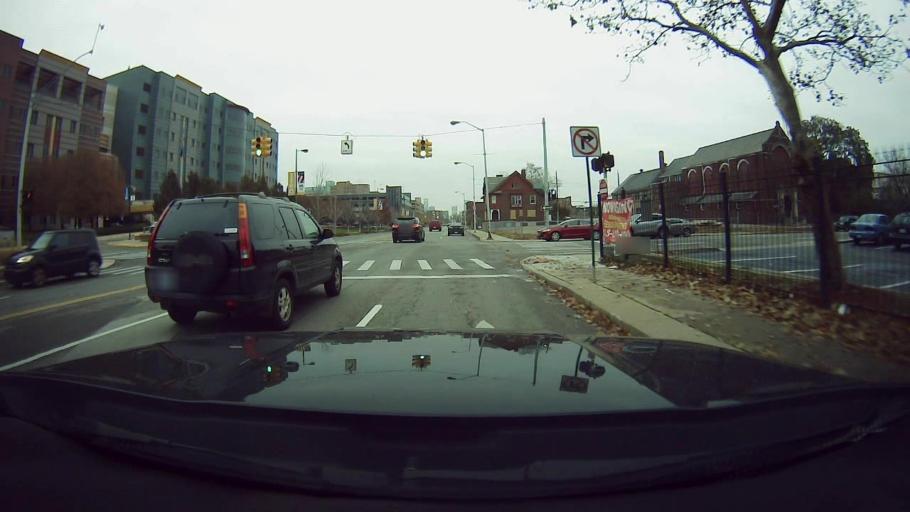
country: US
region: Michigan
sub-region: Wayne County
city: Detroit
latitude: 42.3558
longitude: -83.0610
